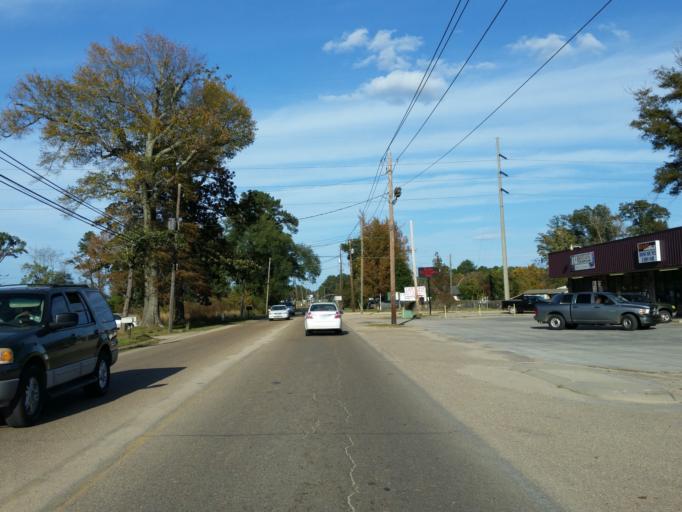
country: US
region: Mississippi
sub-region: Jones County
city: Laurel
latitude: 31.6596
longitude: -89.1644
